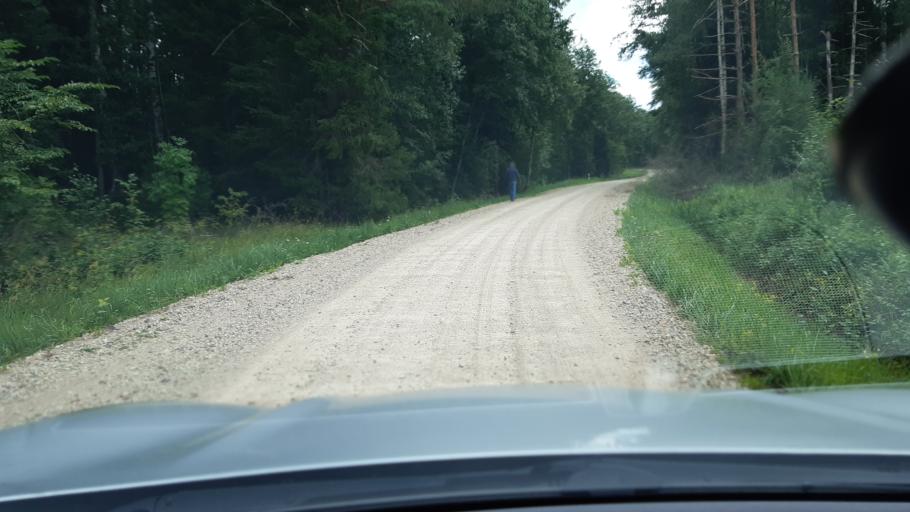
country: EE
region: Raplamaa
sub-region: Jaervakandi vald
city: Jarvakandi
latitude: 58.8071
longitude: 24.8365
